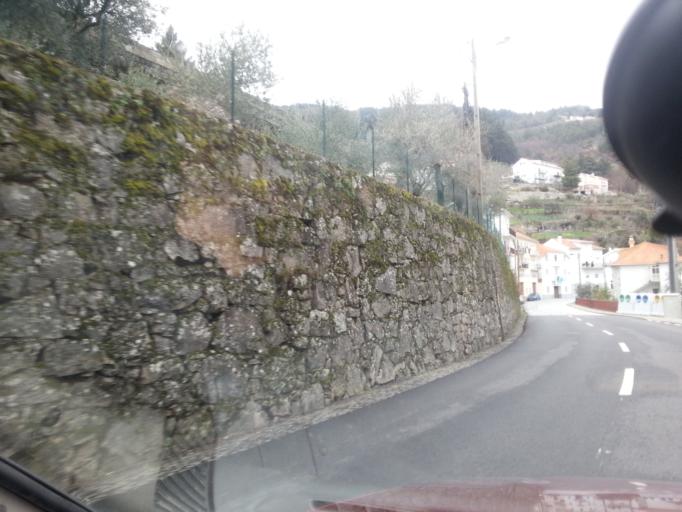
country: PT
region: Guarda
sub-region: Manteigas
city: Manteigas
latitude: 40.3996
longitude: -7.5430
